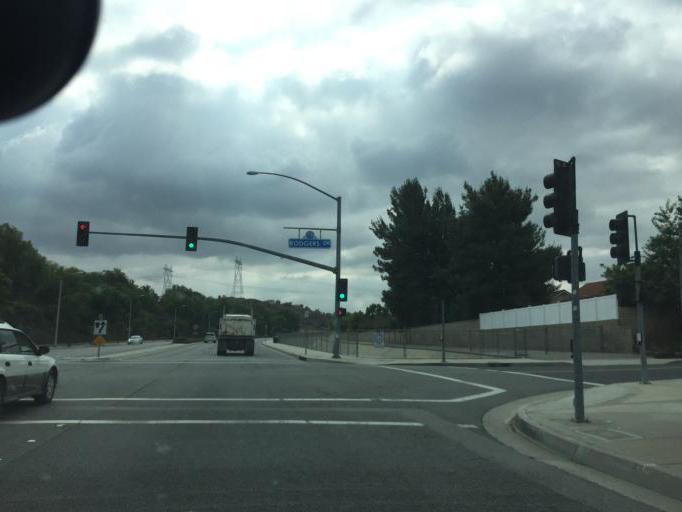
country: US
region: California
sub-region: Los Angeles County
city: Santa Clarita
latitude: 34.4487
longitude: -118.4940
